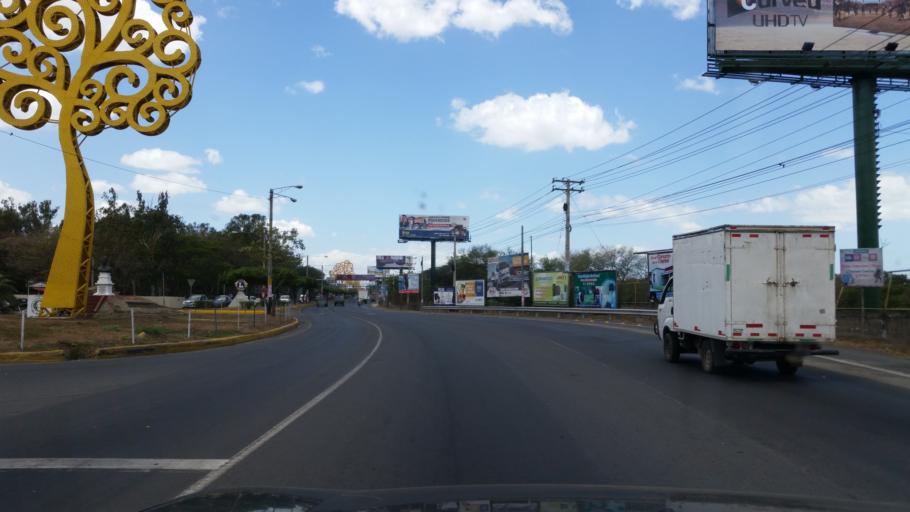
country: NI
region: Managua
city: Managua
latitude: 12.1465
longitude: -86.1799
